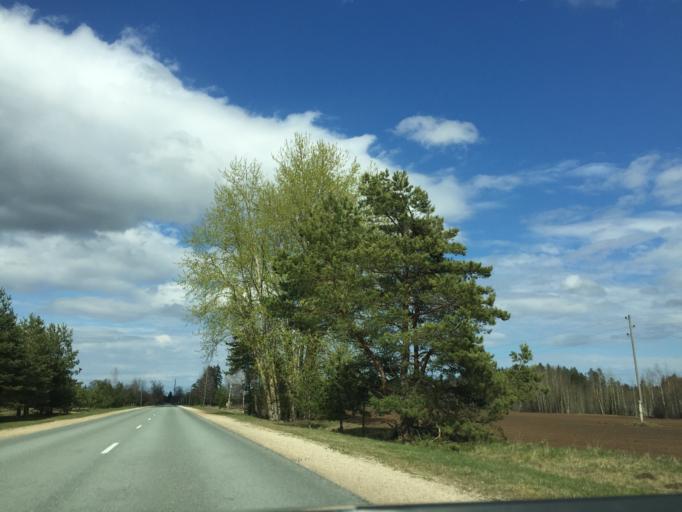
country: LV
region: Gulbenes Rajons
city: Gulbene
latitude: 57.2686
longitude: 26.5659
